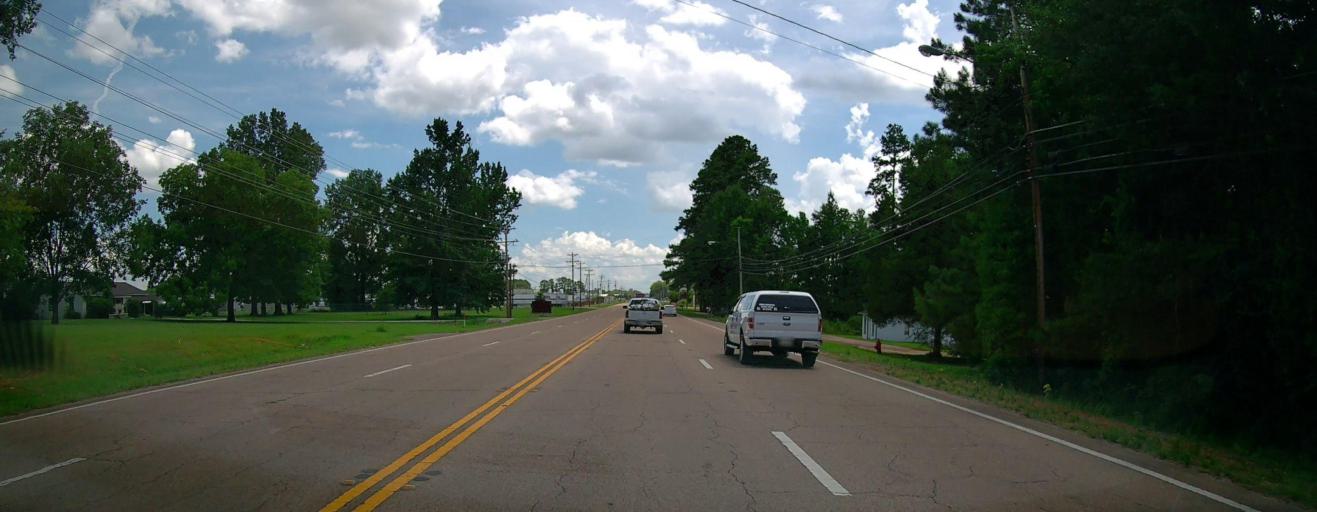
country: US
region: Mississippi
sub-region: Lee County
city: Verona
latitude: 34.1718
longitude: -88.7197
